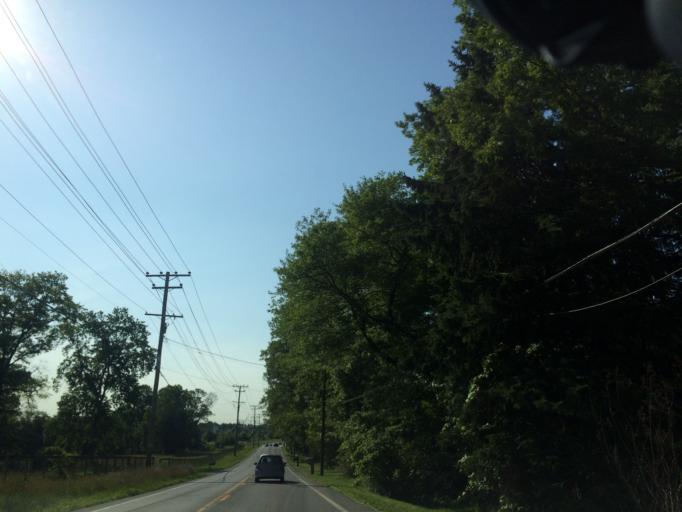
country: US
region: Maryland
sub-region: Howard County
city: Highland
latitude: 39.1657
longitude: -76.9415
